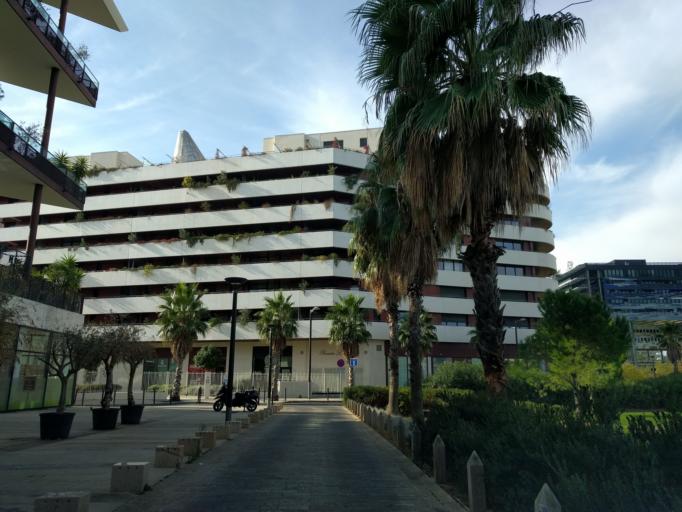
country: FR
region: Languedoc-Roussillon
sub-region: Departement de l'Herault
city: Montpellier
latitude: 43.5985
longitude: 3.8998
